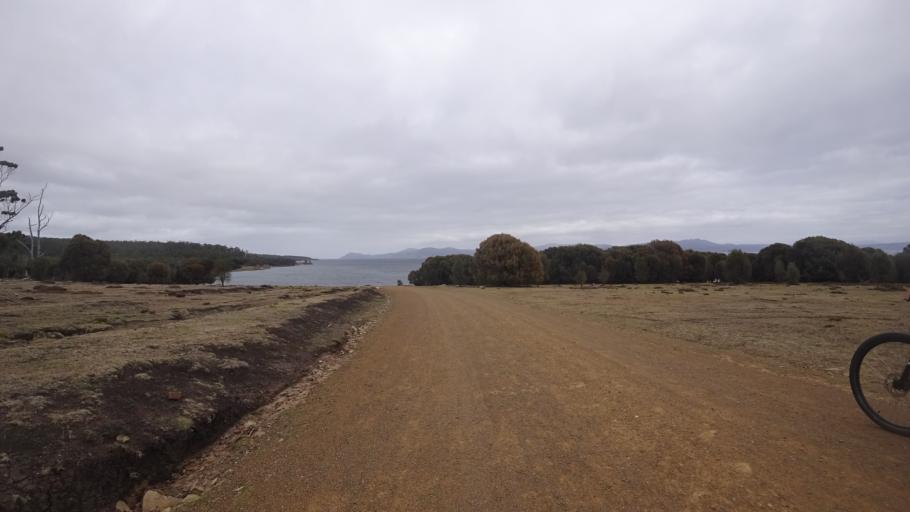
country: AU
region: Tasmania
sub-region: Sorell
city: Sorell
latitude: -42.5850
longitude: 148.0547
